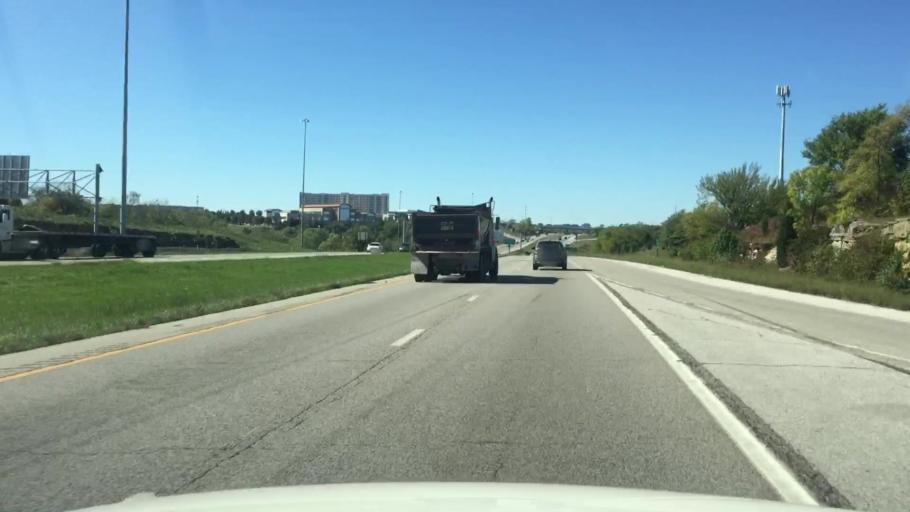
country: US
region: Kansas
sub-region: Johnson County
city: Lenexa
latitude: 38.9421
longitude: -94.7852
